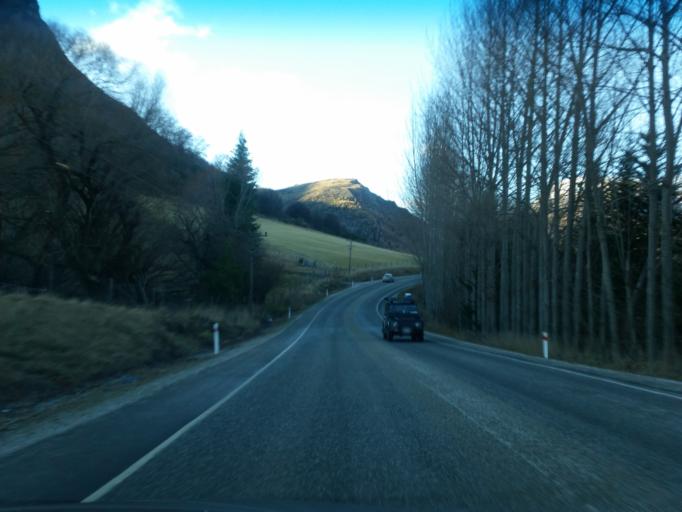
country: NZ
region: Otago
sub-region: Queenstown-Lakes District
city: Arrowtown
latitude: -44.9444
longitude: 168.8060
